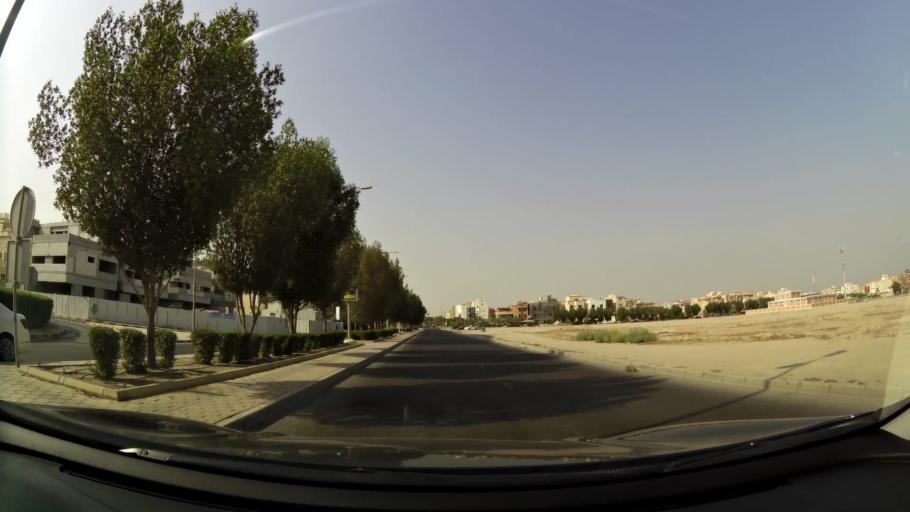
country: KW
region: Mubarak al Kabir
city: Sabah as Salim
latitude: 29.2754
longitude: 48.0447
